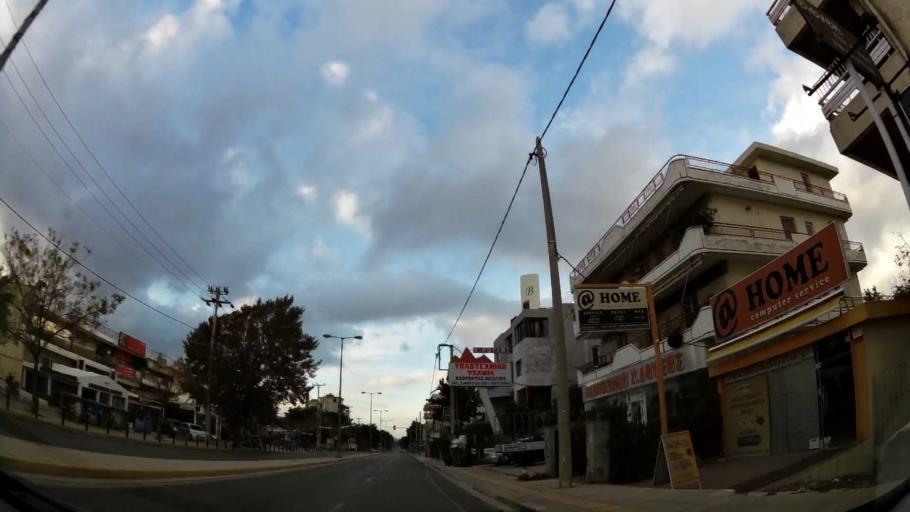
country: GR
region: Attica
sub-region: Nomarchia Athinas
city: Melissia
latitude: 38.0436
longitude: 23.8353
